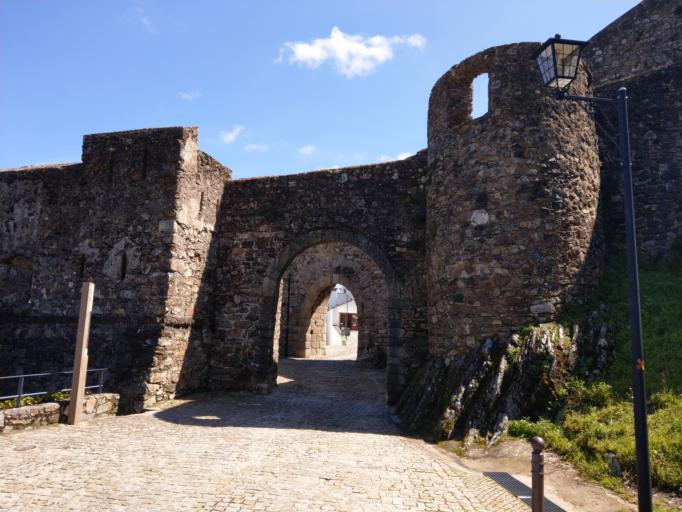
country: PT
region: Portalegre
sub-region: Marvao
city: Marvao
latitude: 39.3958
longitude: -7.3774
